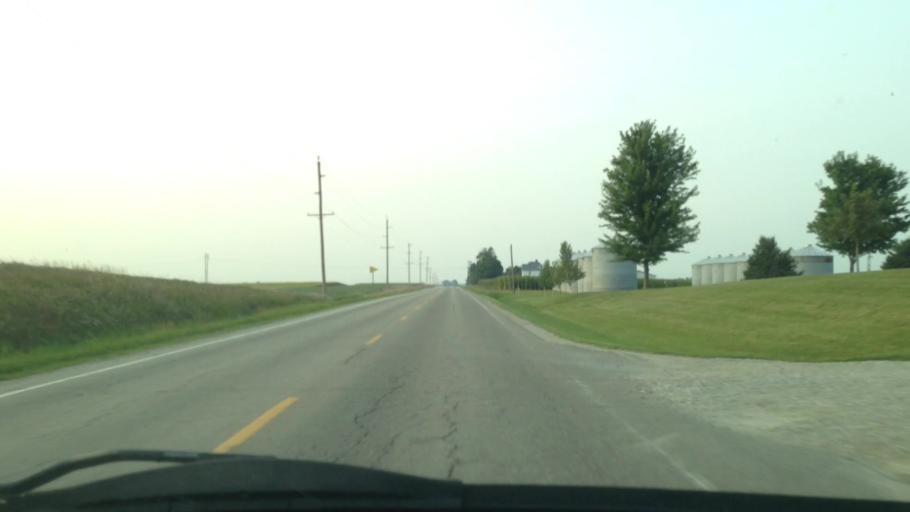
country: US
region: Iowa
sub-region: Iowa County
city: Marengo
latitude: 41.9378
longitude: -92.0848
